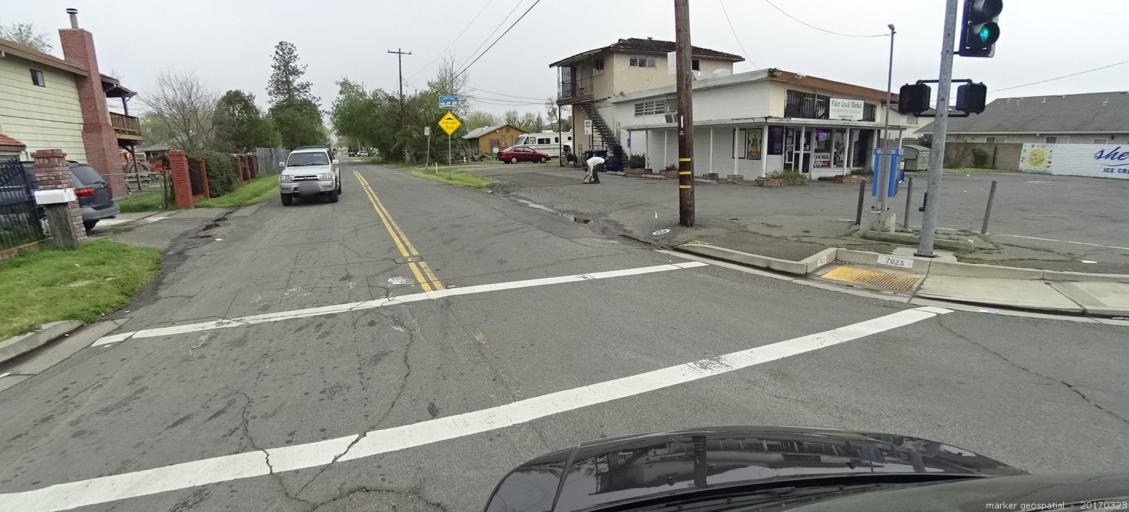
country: US
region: California
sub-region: Sacramento County
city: Florin
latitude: 38.5107
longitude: -121.4224
